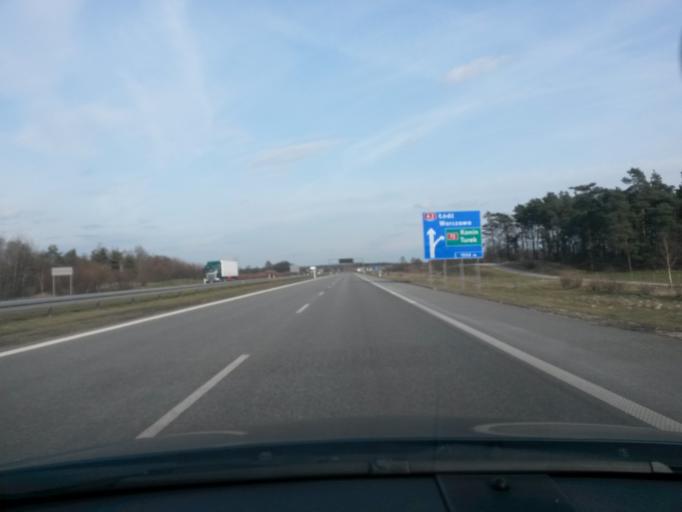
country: PL
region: Greater Poland Voivodeship
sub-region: Powiat koninski
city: Stare Miasto
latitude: 52.1605
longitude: 18.2367
